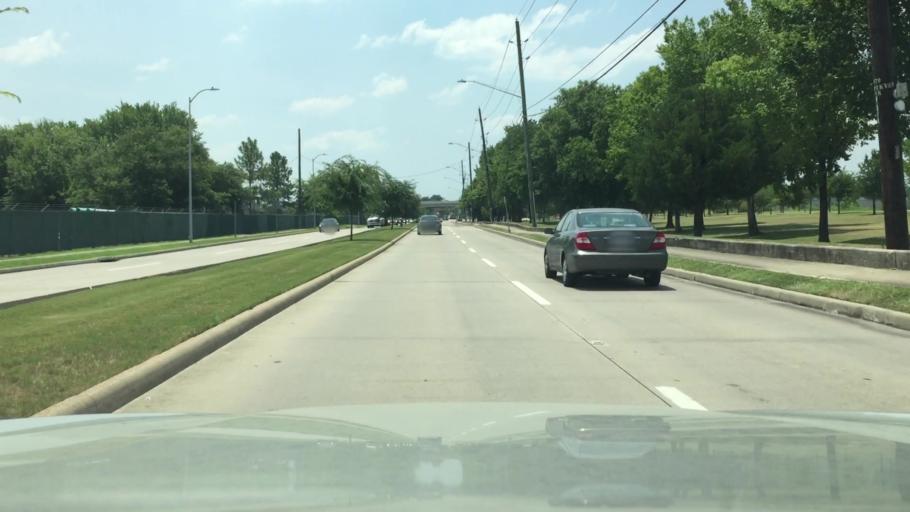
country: US
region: Texas
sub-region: Fort Bend County
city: Meadows Place
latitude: 29.7192
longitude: -95.5923
